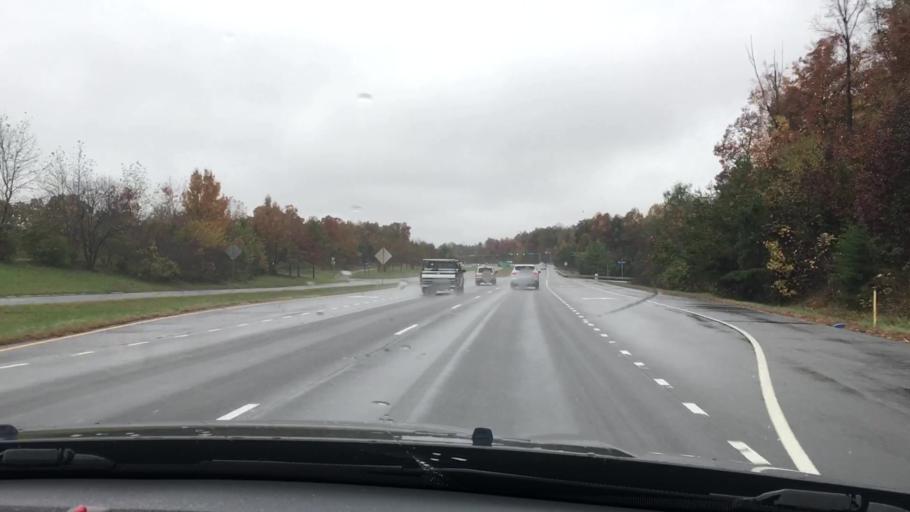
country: US
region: Virginia
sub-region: Prince William County
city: Lake Ridge
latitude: 38.7323
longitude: -77.2799
